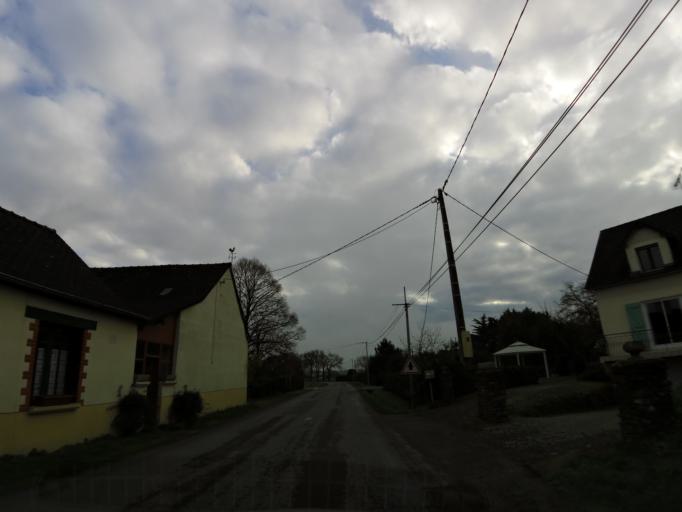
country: FR
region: Brittany
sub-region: Departement d'Ille-et-Vilaine
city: Chanteloup
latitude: 47.9695
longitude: -1.6457
